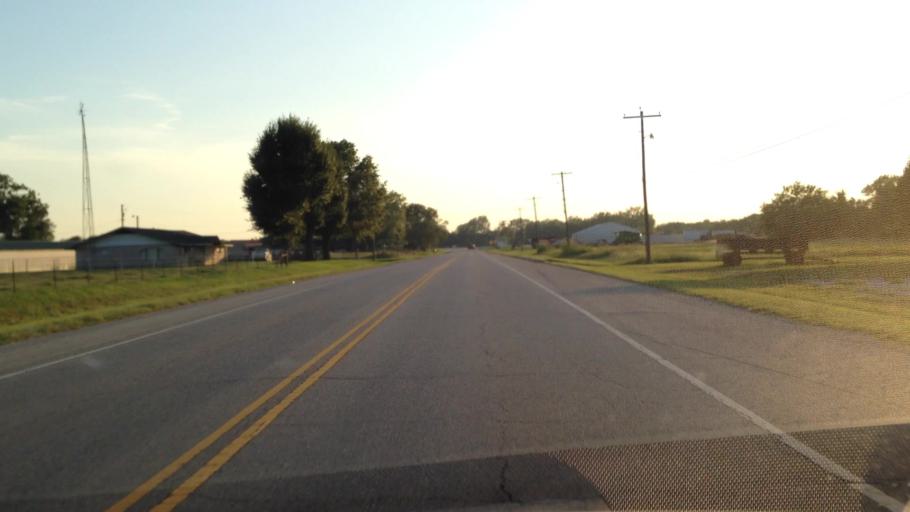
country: US
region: Oklahoma
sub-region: Ottawa County
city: Afton
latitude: 36.6884
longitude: -94.9749
